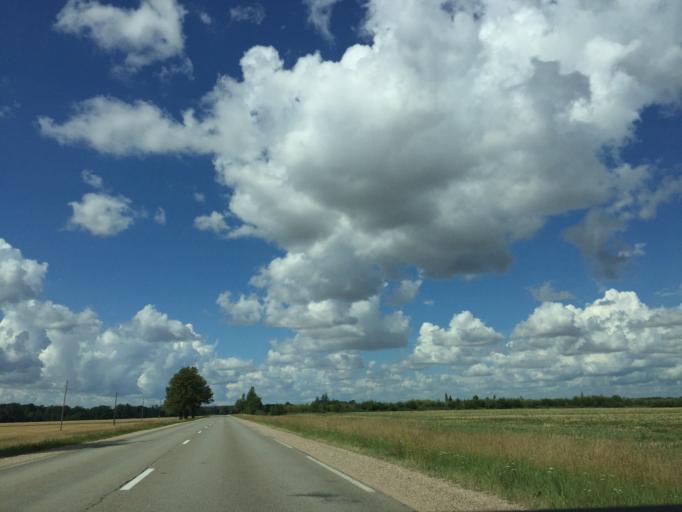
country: LV
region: Bauskas Rajons
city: Bauska
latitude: 56.3967
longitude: 24.1466
